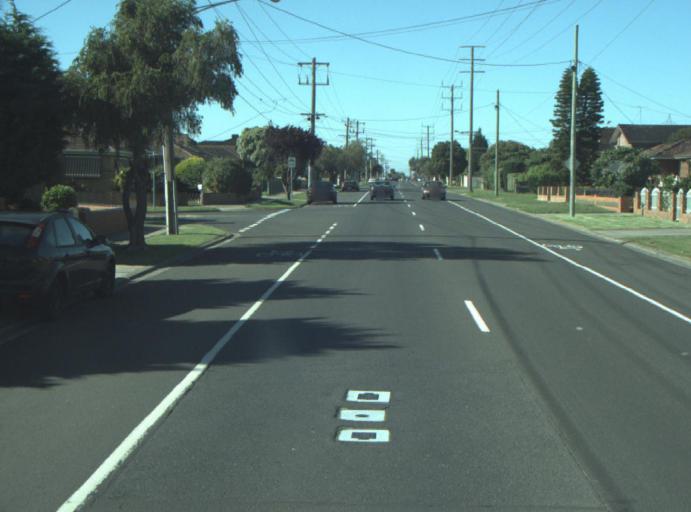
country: AU
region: Victoria
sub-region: Greater Geelong
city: Bell Post Hill
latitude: -38.0979
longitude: 144.3235
